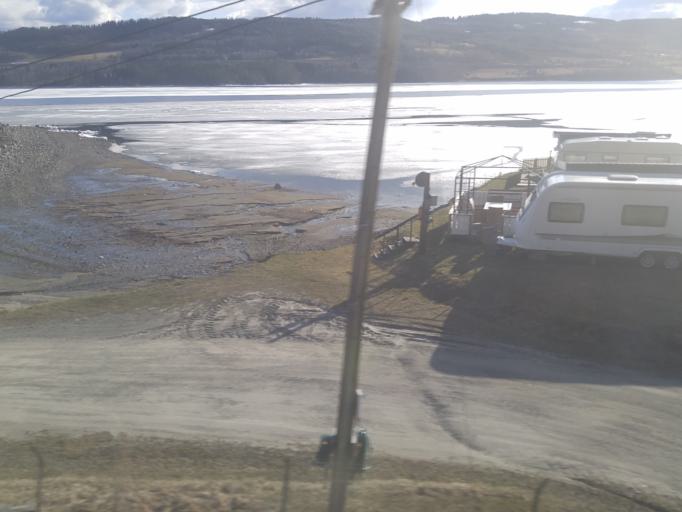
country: NO
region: Hedmark
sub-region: Ringsaker
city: Moelv
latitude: 60.9939
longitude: 10.5990
